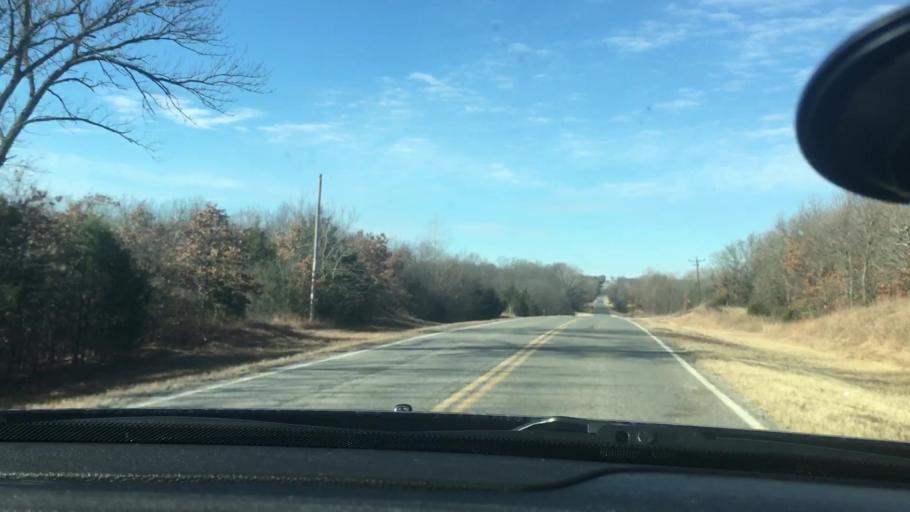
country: US
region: Oklahoma
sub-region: Seminole County
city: Konawa
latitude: 34.9858
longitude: -96.8776
